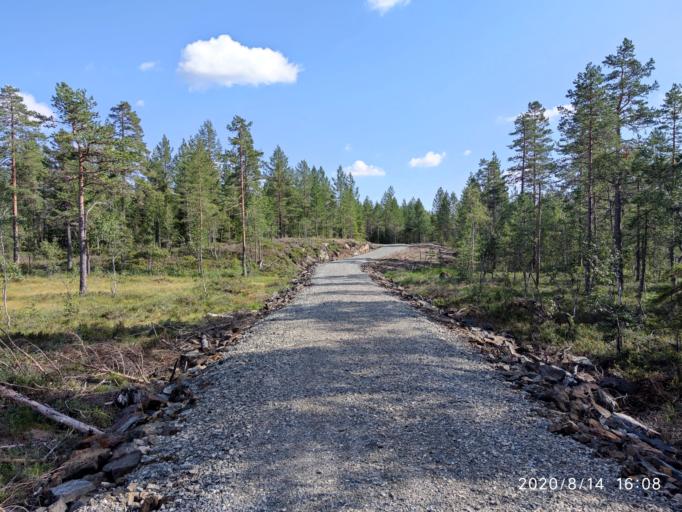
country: NO
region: Akershus
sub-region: Nittedal
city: Aneby
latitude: 60.1437
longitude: 10.8984
